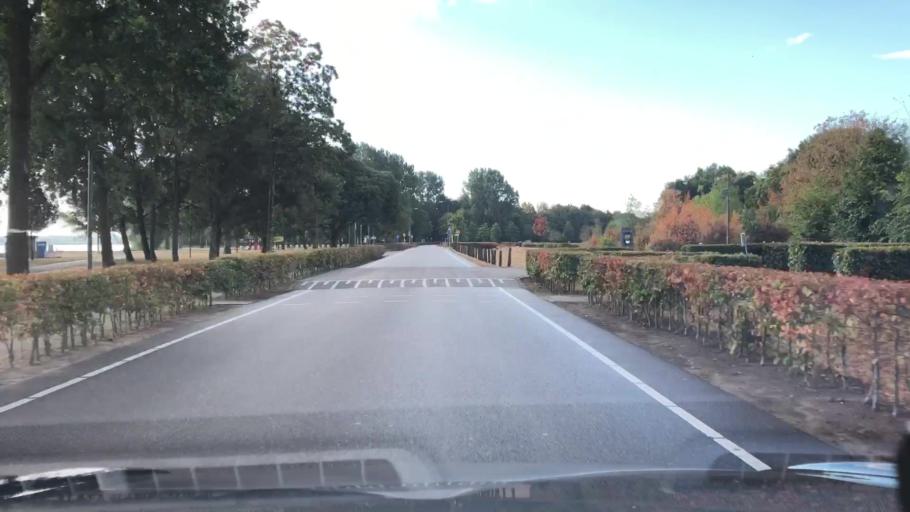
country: NL
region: North Holland
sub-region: Gemeente Naarden
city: Naarden
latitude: 52.3169
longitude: 5.1442
